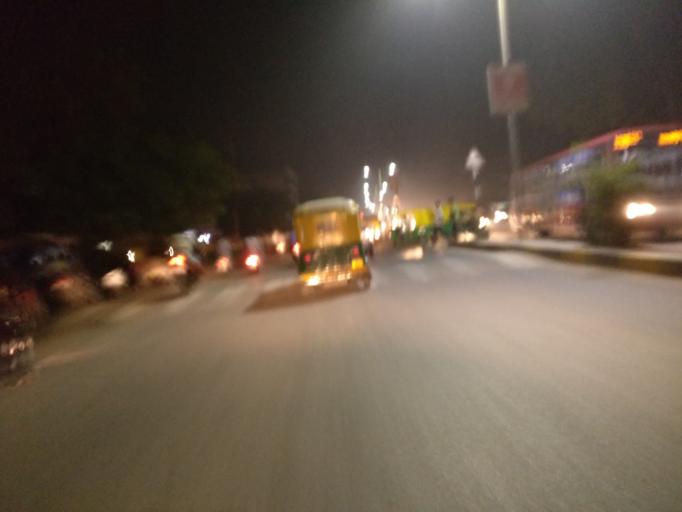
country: IN
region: Gujarat
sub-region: Ahmadabad
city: Sarkhej
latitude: 22.9999
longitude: 72.5462
